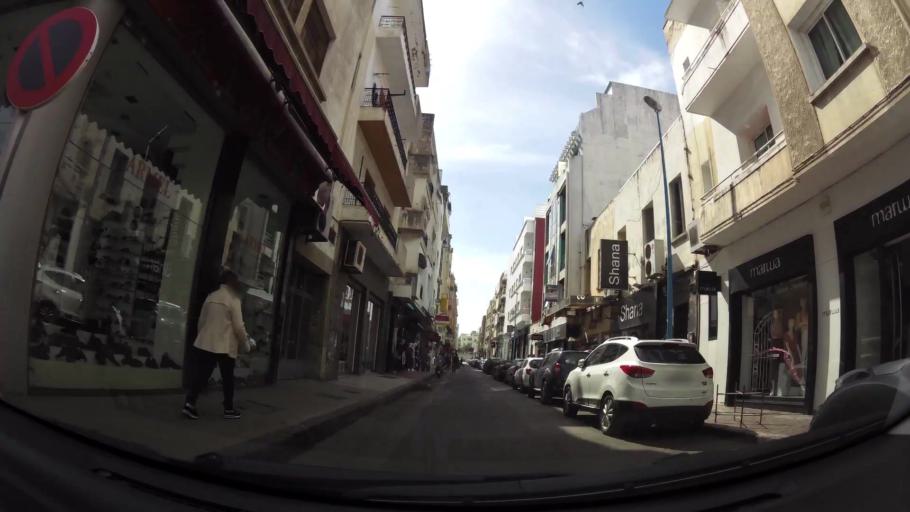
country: MA
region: Grand Casablanca
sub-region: Casablanca
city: Casablanca
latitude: 33.5850
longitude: -7.6338
